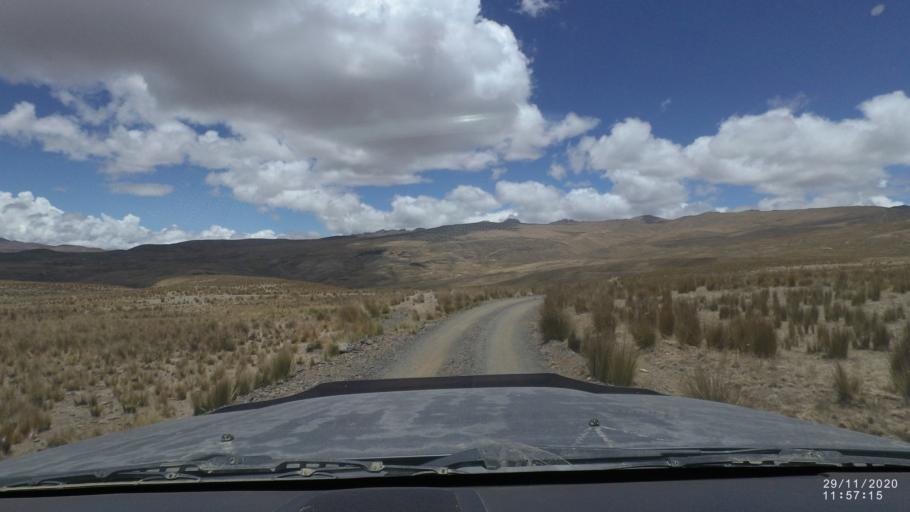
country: BO
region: Cochabamba
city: Cochabamba
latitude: -17.1597
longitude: -66.2741
